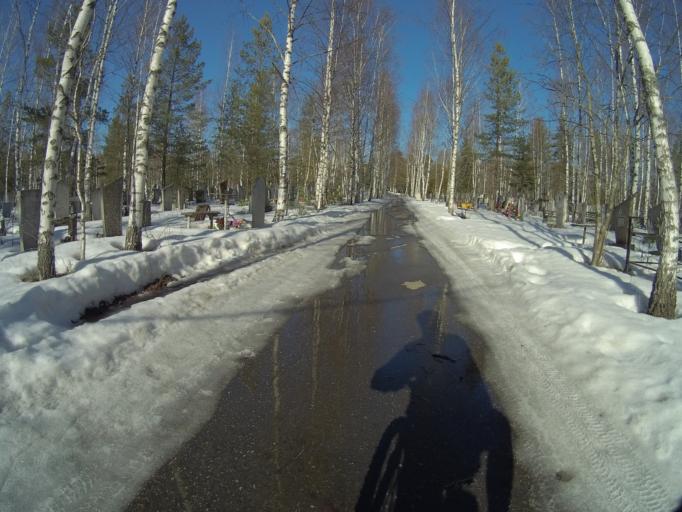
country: RU
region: Vladimir
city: Kommunar
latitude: 56.0401
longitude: 40.4331
